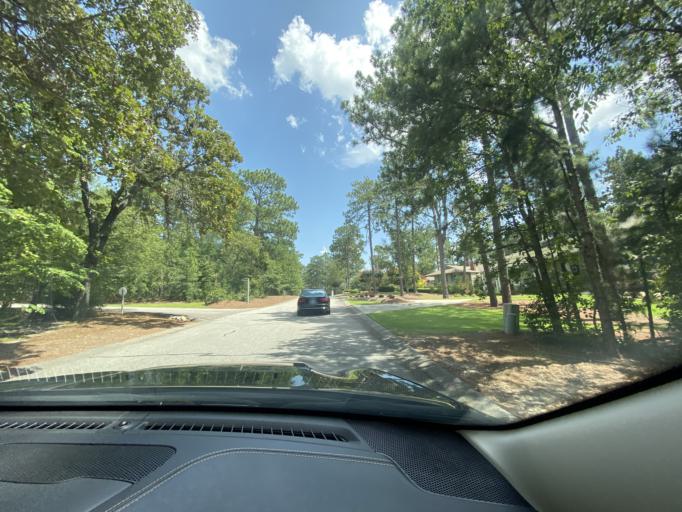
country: US
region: North Carolina
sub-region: Moore County
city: Pinehurst
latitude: 35.1981
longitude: -79.4389
